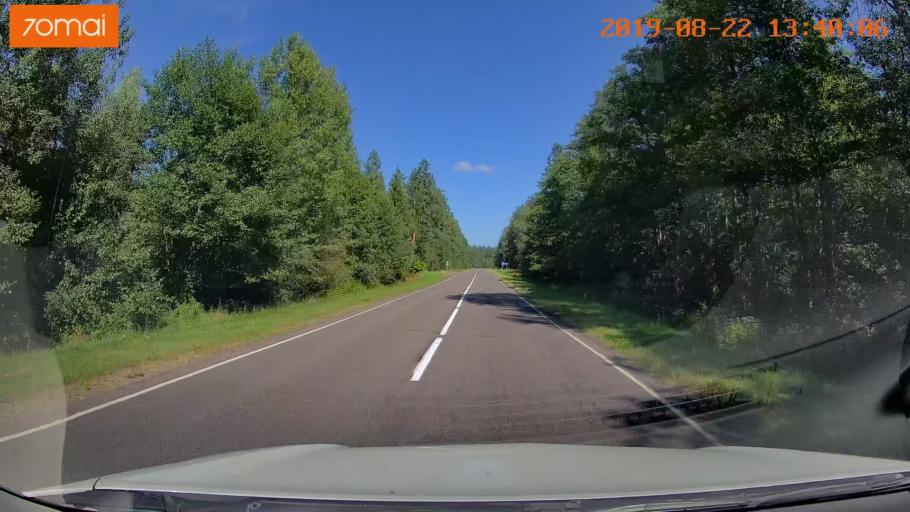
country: BY
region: Minsk
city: Staryya Darohi
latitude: 53.2330
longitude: 28.3608
